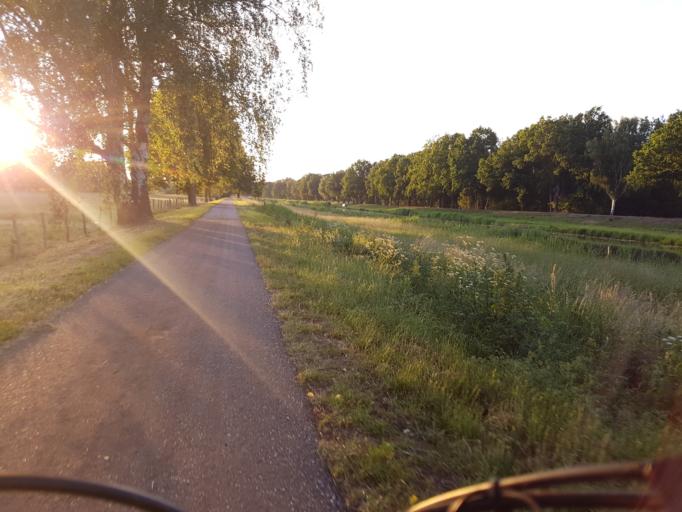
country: DE
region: Brandenburg
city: Schilda
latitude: 51.5770
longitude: 13.3458
